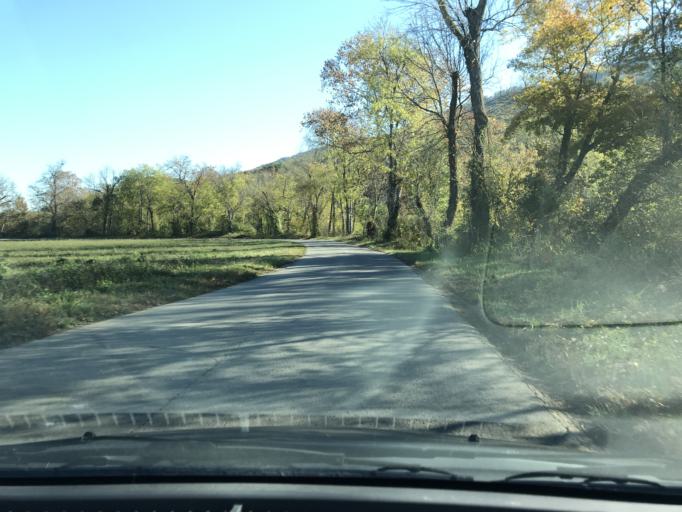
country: US
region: Georgia
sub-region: Dade County
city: Trenton
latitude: 34.8981
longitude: -85.4630
